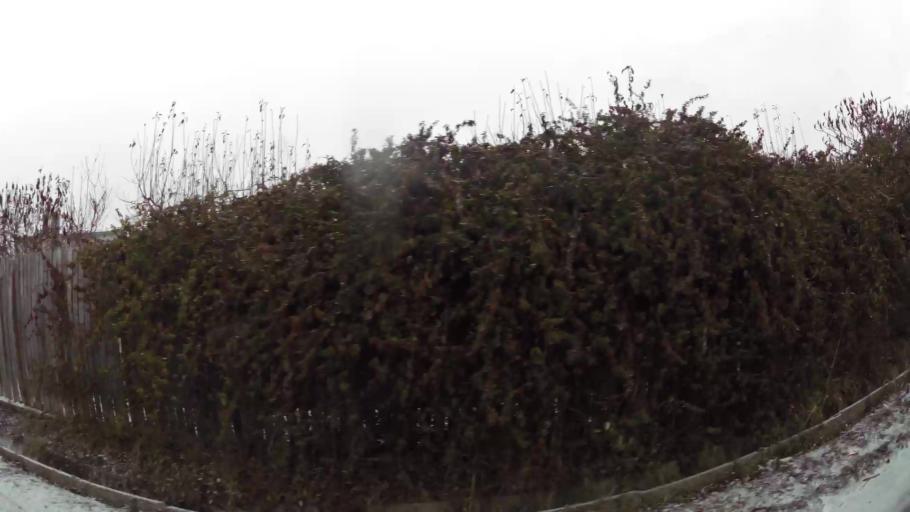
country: RO
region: Dambovita
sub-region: Comuna Aninoasa
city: Viforata
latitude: 44.9452
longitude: 25.4677
